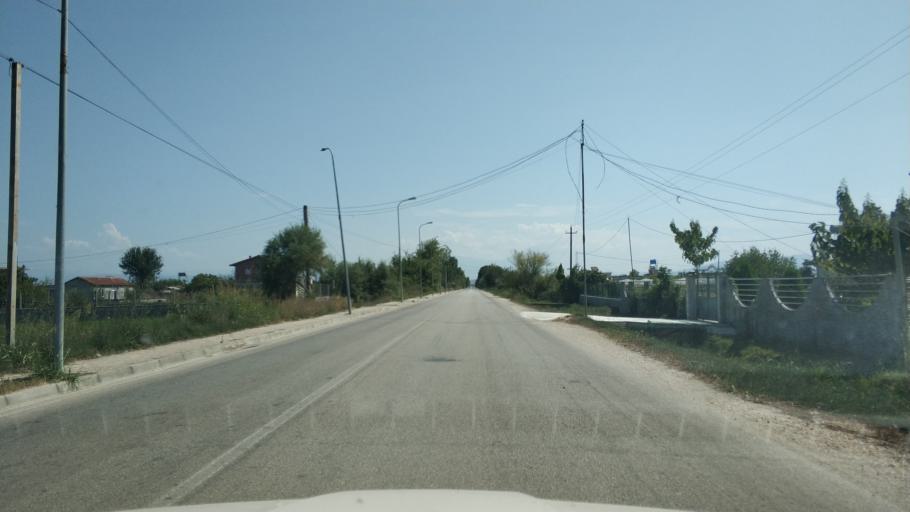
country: AL
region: Fier
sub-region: Rrethi i Lushnjes
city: Krutja e Poshtme
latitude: 40.8887
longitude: 19.6451
